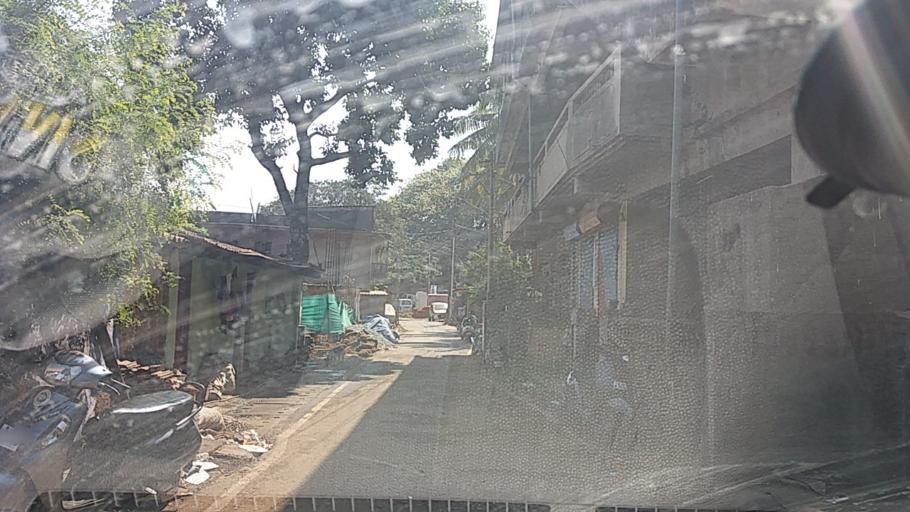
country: IN
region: Goa
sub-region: South Goa
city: Marmagao
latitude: 15.4078
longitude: 73.7938
